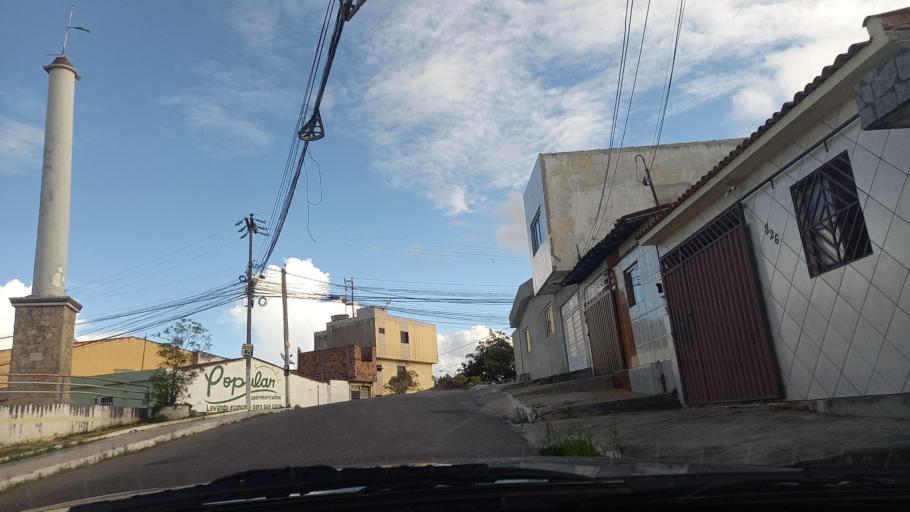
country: BR
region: Pernambuco
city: Garanhuns
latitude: -8.8989
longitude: -36.4953
